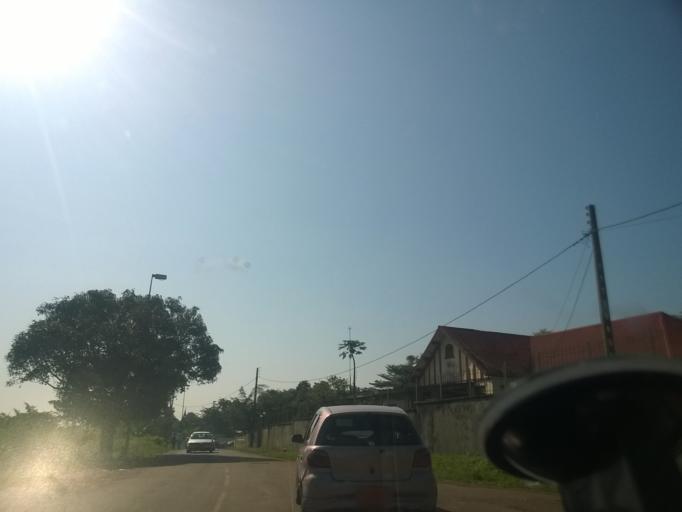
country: CM
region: Centre
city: Yaounde
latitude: 3.8553
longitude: 11.5113
